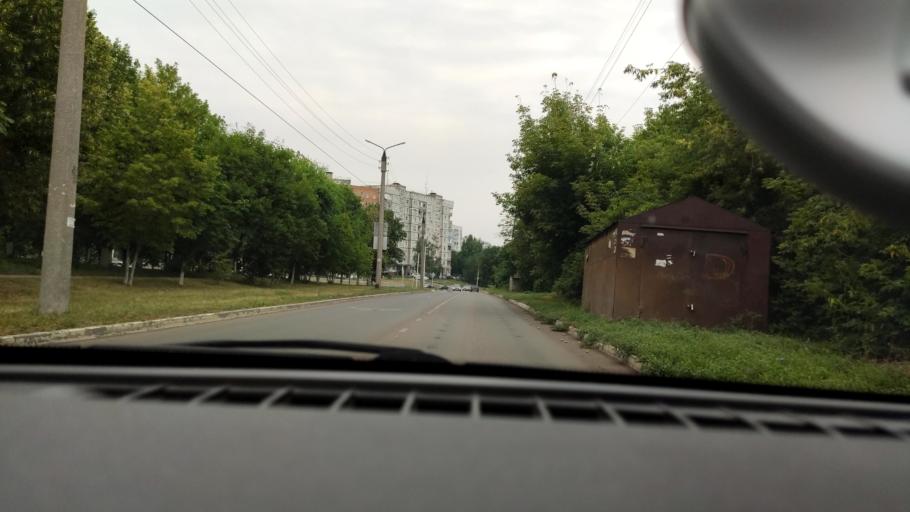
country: RU
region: Samara
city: Novokuybyshevsk
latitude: 53.0971
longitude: 49.9846
